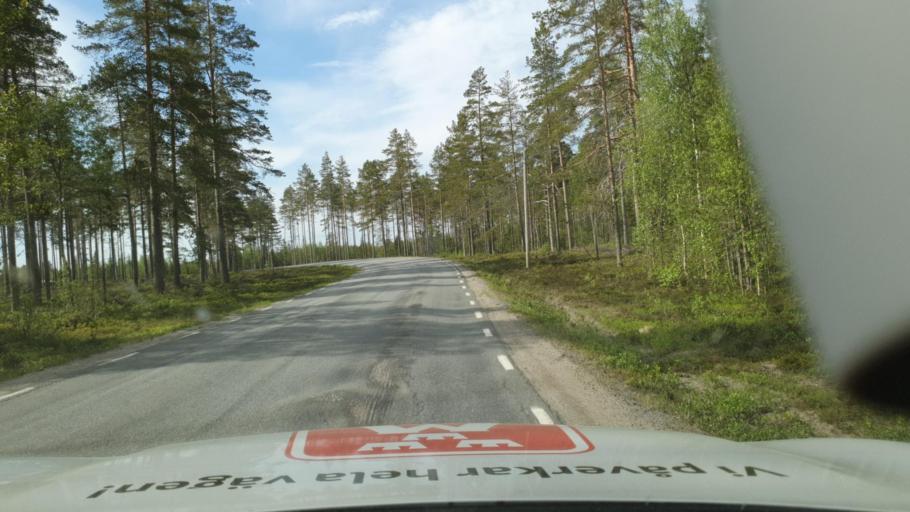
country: SE
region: Vaesterbotten
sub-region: Umea Kommun
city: Roback
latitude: 63.7021
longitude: 20.1504
